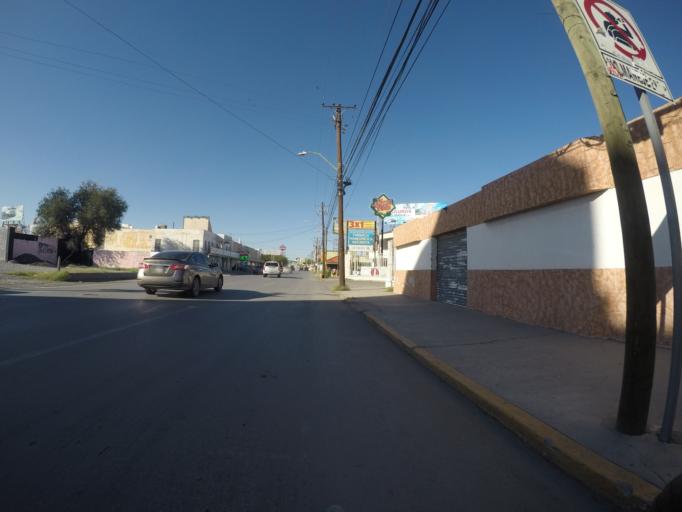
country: MX
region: Chihuahua
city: Ciudad Juarez
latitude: 31.7376
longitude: -106.4244
